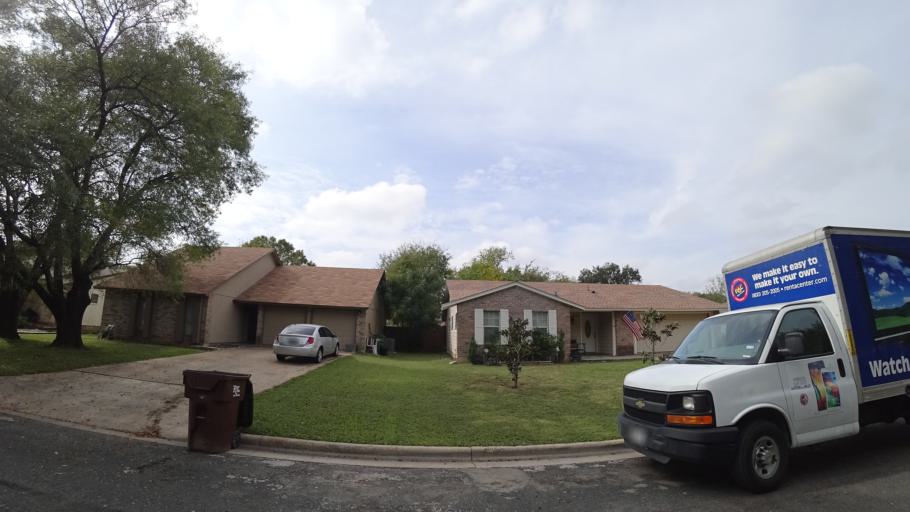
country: US
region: Texas
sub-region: Williamson County
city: Round Rock
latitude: 30.4969
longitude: -97.6820
